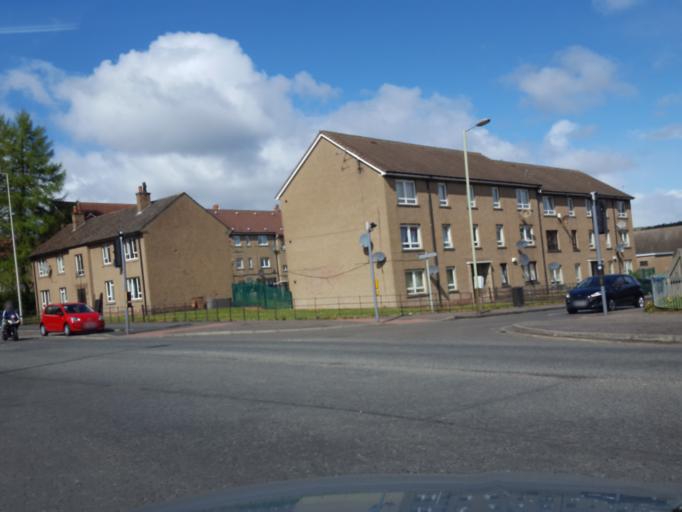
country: GB
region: Scotland
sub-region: Angus
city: Muirhead
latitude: 56.4715
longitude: -3.0445
